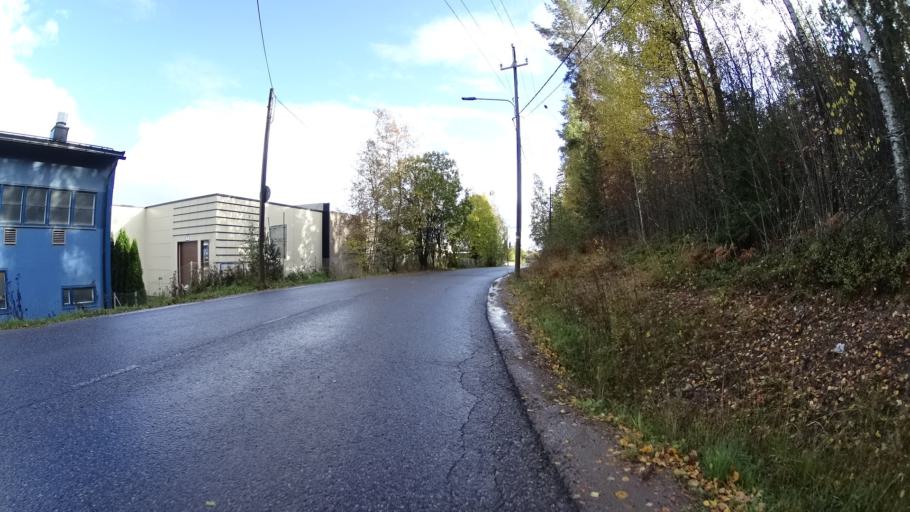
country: FI
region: Uusimaa
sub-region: Helsinki
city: Kilo
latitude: 60.2861
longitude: 24.8144
